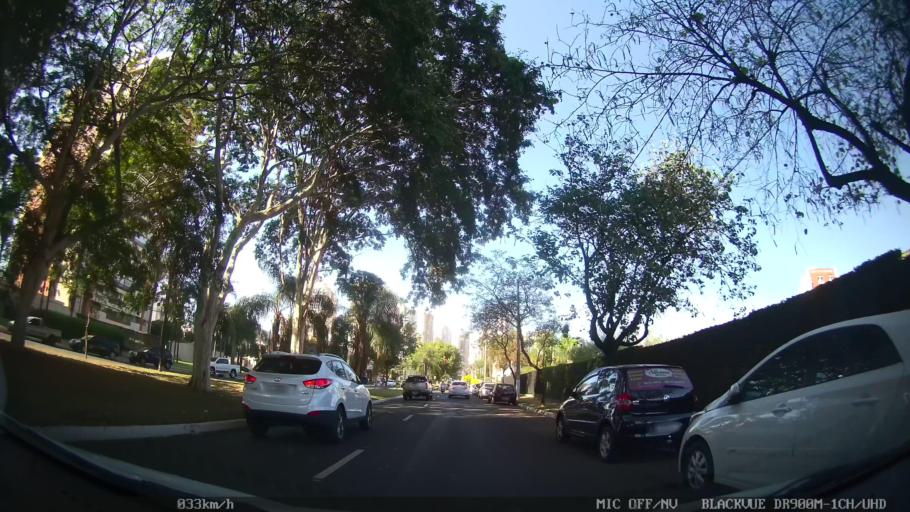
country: BR
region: Sao Paulo
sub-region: Ribeirao Preto
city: Ribeirao Preto
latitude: -21.2095
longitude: -47.8071
